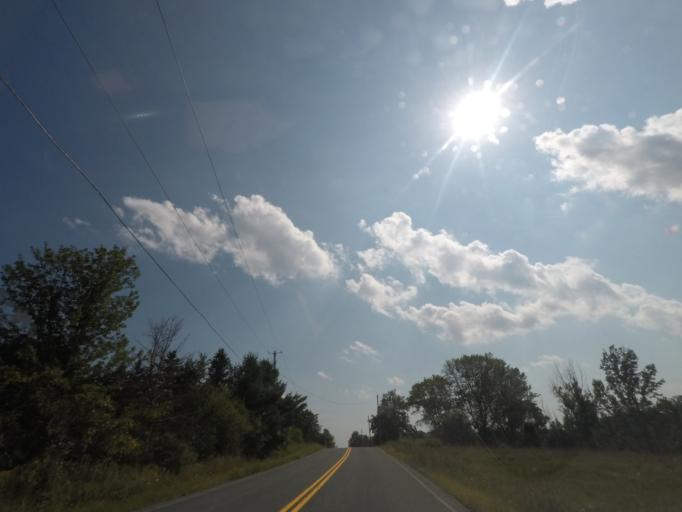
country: US
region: New York
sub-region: Rensselaer County
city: Averill Park
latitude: 42.6496
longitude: -73.5260
